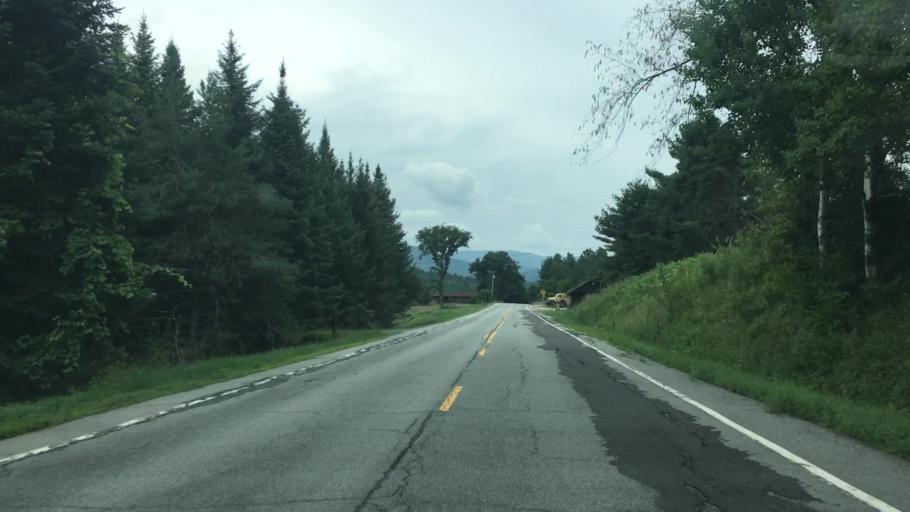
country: US
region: New York
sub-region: Essex County
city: Elizabethtown
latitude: 44.3916
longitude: -73.7100
